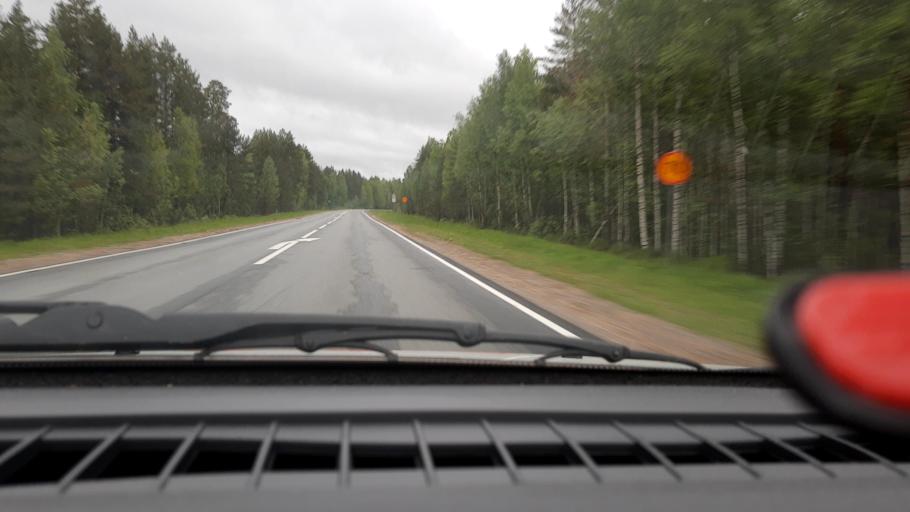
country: RU
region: Nizjnij Novgorod
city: Krasnyye Baki
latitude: 57.2087
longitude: 45.4617
